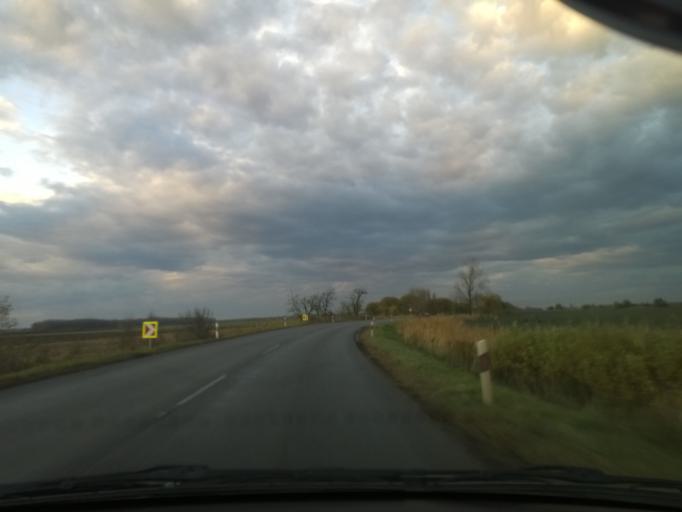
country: HU
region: Bacs-Kiskun
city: Apostag
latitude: 46.8494
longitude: 18.9954
